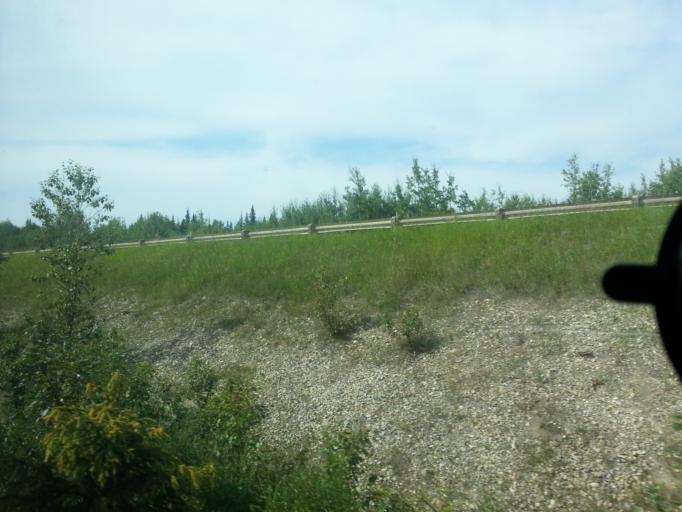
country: CA
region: Alberta
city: Edson
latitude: 53.5287
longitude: -116.8377
